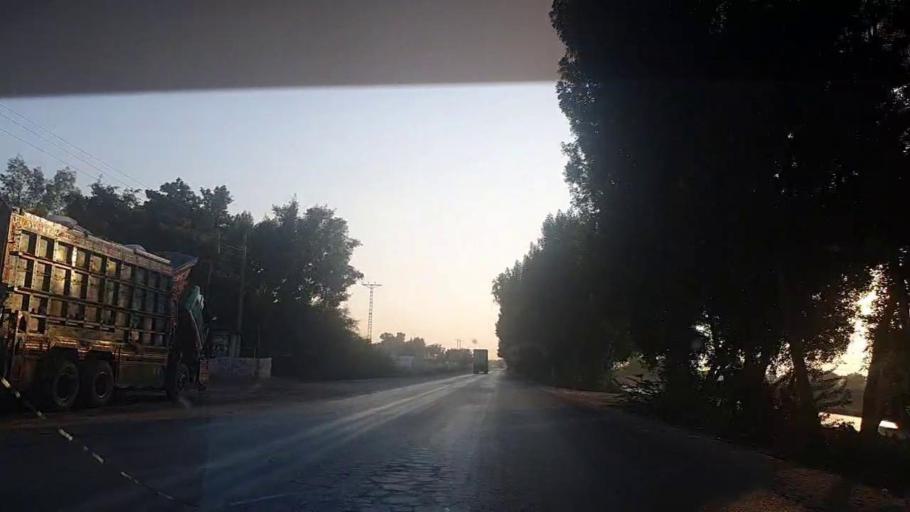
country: PK
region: Sindh
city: Hingorja
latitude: 27.1856
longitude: 68.4030
